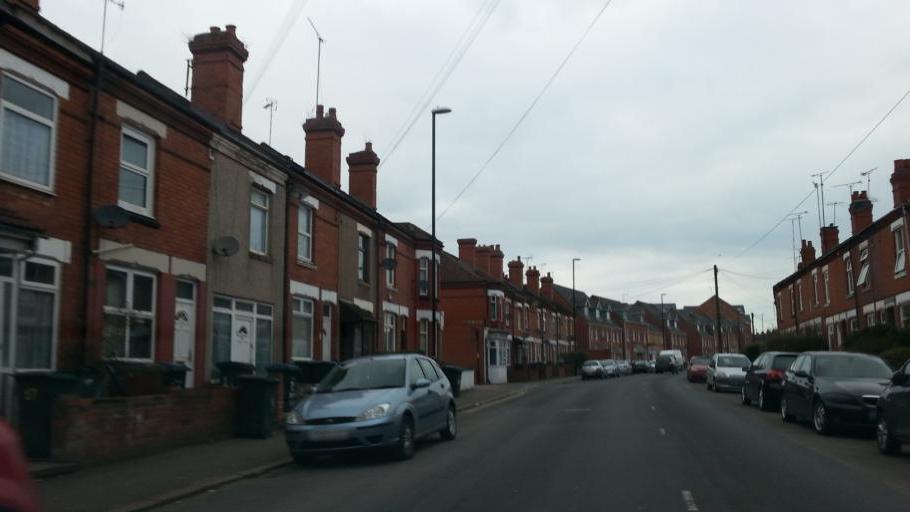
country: GB
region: England
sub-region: Coventry
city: Coventry
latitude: 52.4106
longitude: -1.4888
